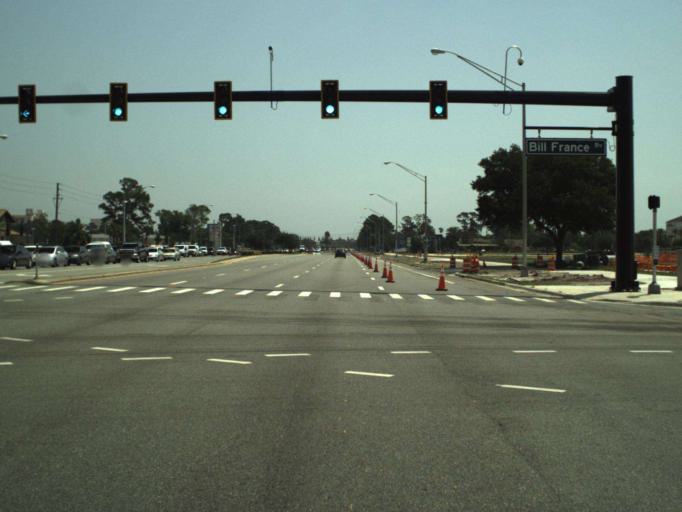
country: US
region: Florida
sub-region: Volusia County
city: Daytona Beach
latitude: 29.1928
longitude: -81.0669
